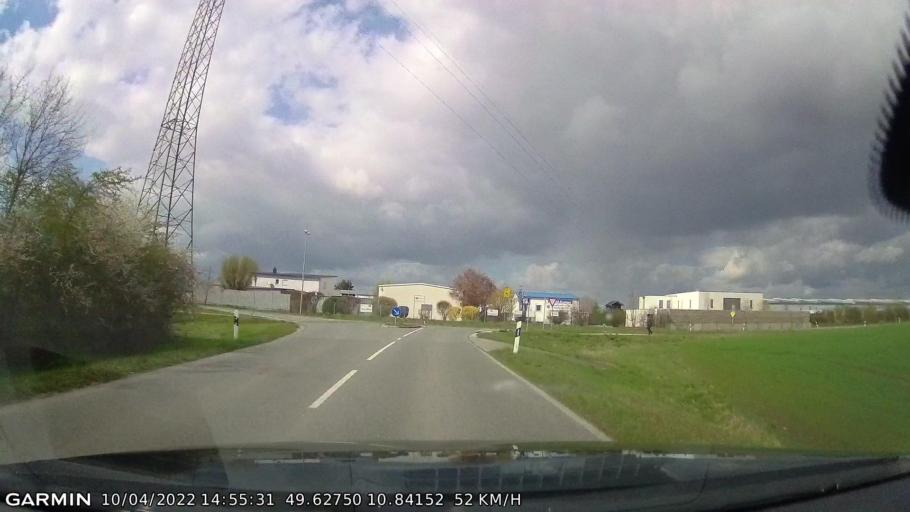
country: DE
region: Bavaria
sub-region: Regierungsbezirk Mittelfranken
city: Weisendorf
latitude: 49.6276
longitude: 10.8415
